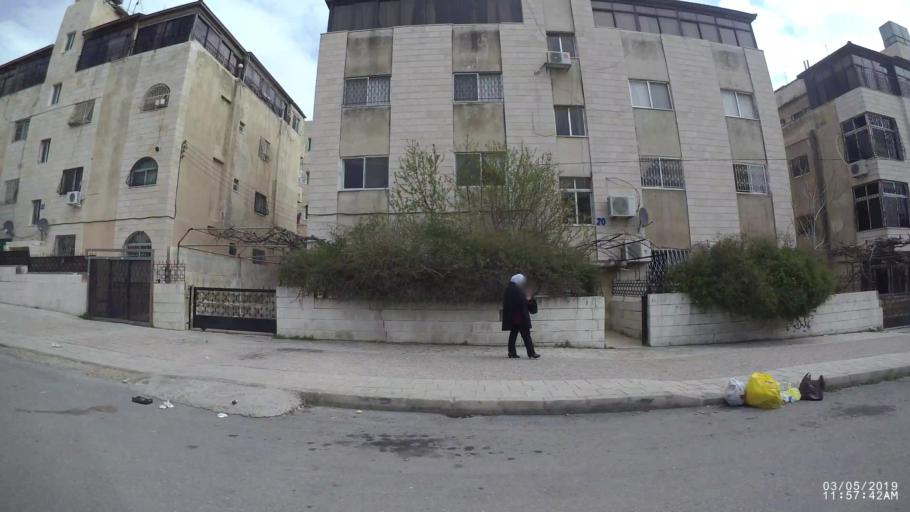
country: JO
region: Amman
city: Amman
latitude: 31.9738
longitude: 35.9296
